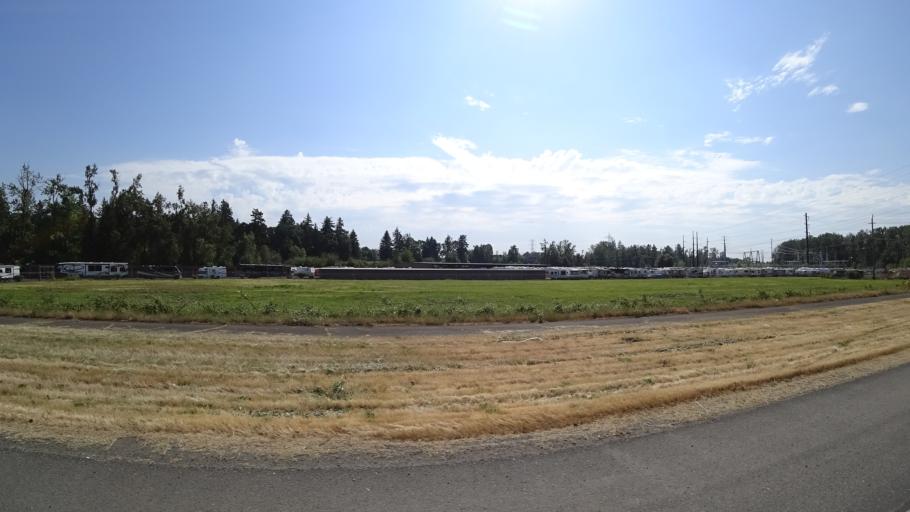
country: US
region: Oregon
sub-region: Multnomah County
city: Fairview
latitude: 45.5541
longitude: -122.4248
